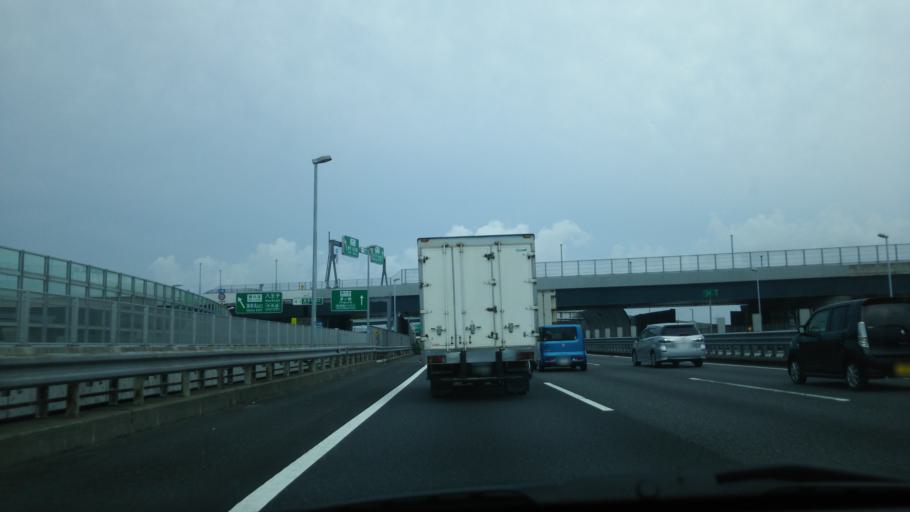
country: JP
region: Kanagawa
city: Atsugi
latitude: 35.4226
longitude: 139.3736
